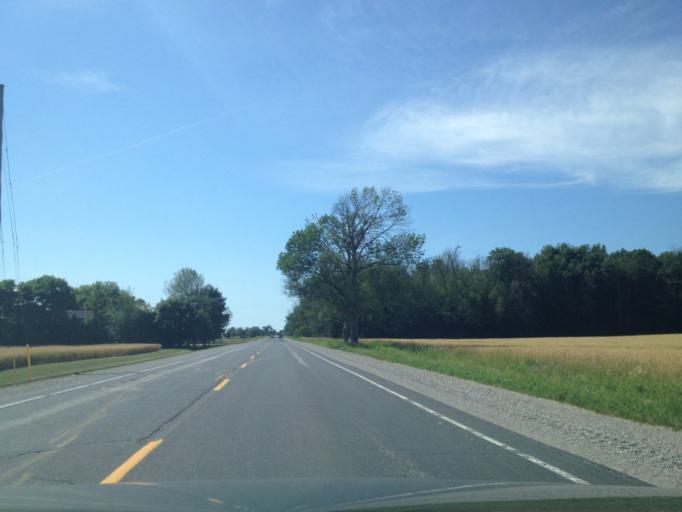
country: CA
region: Ontario
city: Stratford
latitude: 43.4936
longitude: -80.8581
